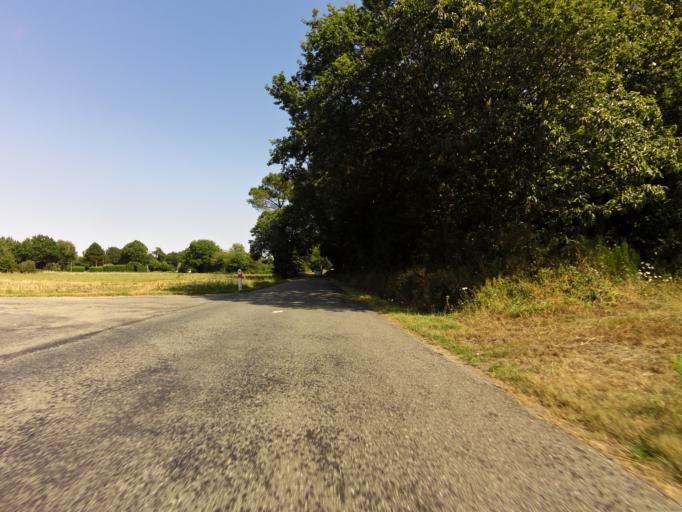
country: FR
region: Brittany
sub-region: Departement du Morbihan
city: Limerzel
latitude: 47.6440
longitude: -2.3676
